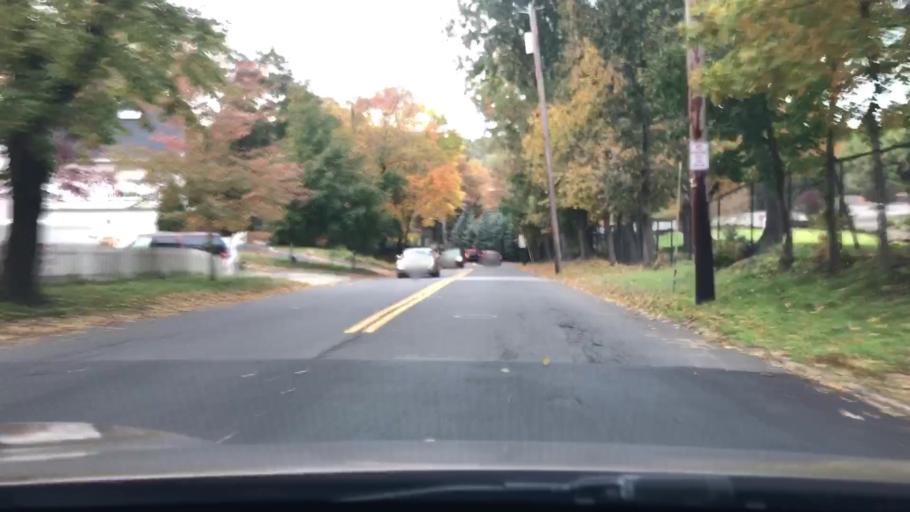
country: US
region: New York
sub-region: Westchester County
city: Tuckahoe
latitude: 40.9678
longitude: -73.8145
